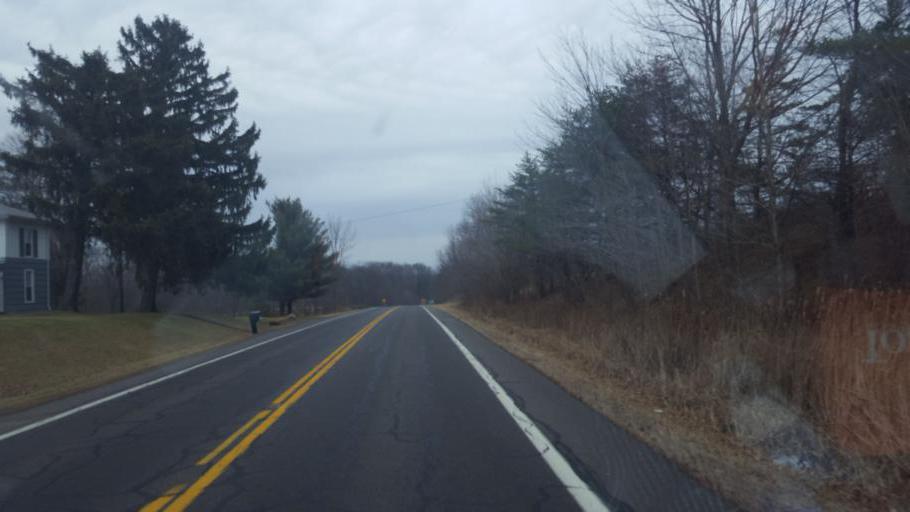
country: US
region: Ohio
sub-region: Crawford County
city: Galion
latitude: 40.6729
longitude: -82.8209
